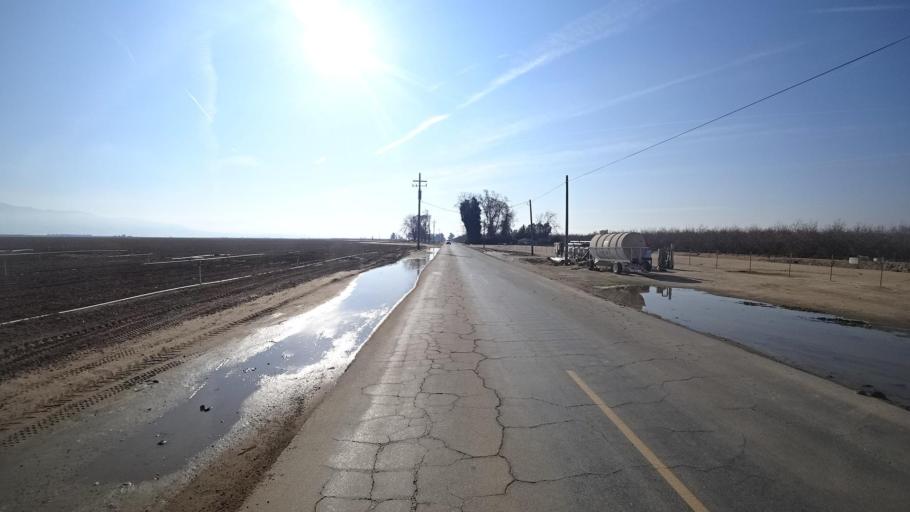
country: US
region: California
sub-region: Kern County
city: Lamont
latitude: 35.2492
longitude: -118.8961
